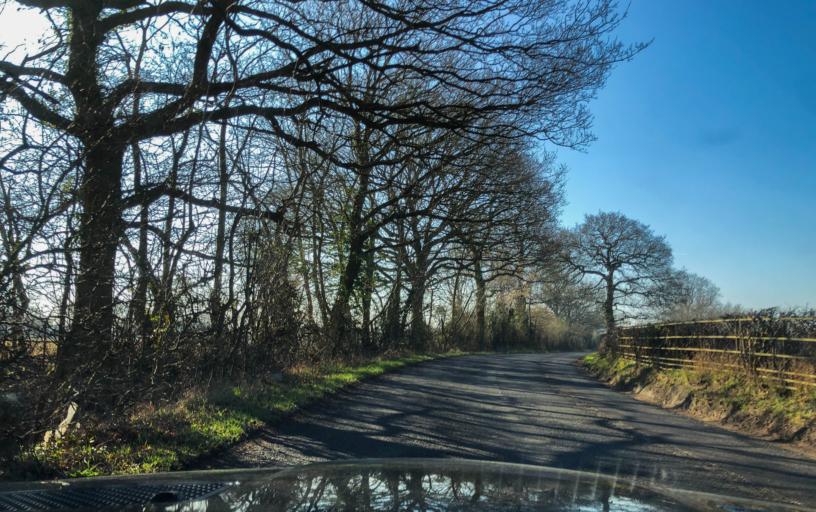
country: GB
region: England
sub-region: Warwickshire
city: Wellesbourne Mountford
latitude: 52.2318
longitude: -1.5598
